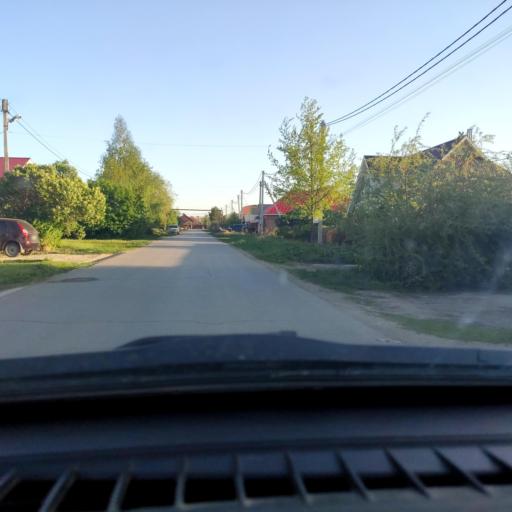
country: RU
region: Samara
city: Tol'yatti
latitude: 53.5575
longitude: 49.4014
